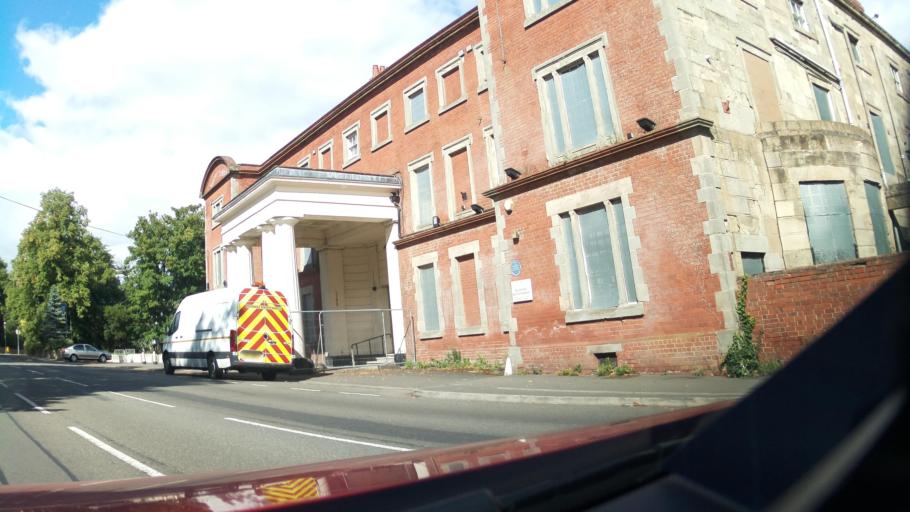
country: GB
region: England
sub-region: Leicestershire
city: Ashby de la Zouch
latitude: 52.7440
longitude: -1.4744
